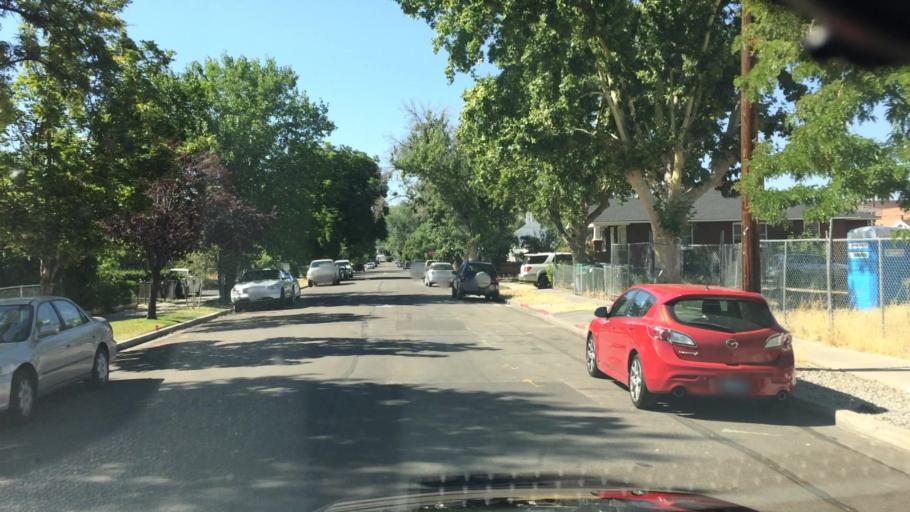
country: US
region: Nevada
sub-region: Washoe County
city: Reno
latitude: 39.5133
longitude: -119.8083
